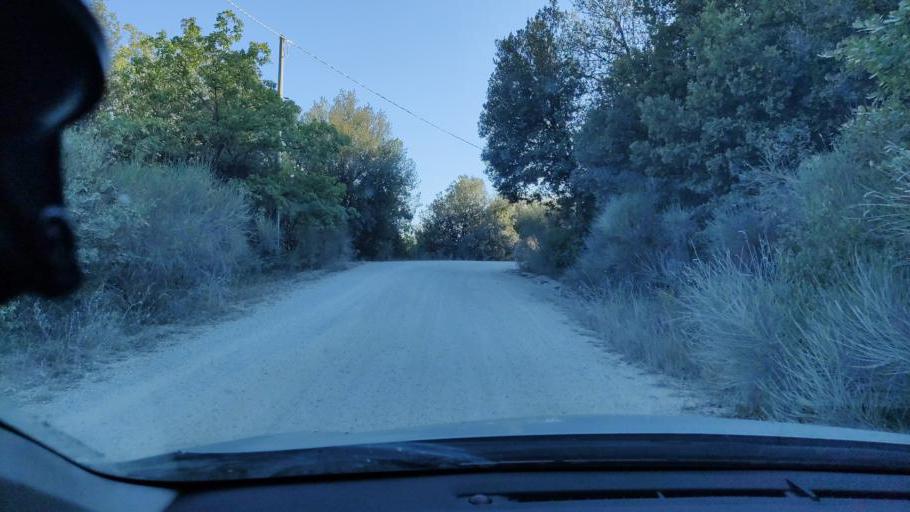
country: IT
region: Umbria
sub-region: Provincia di Terni
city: Amelia
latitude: 42.5386
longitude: 12.3833
